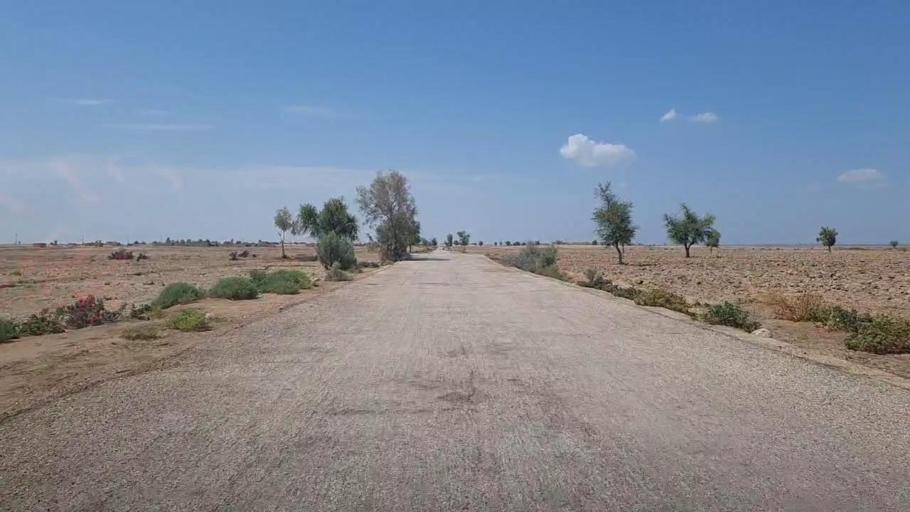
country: PK
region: Sindh
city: Sehwan
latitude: 26.3406
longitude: 67.6747
